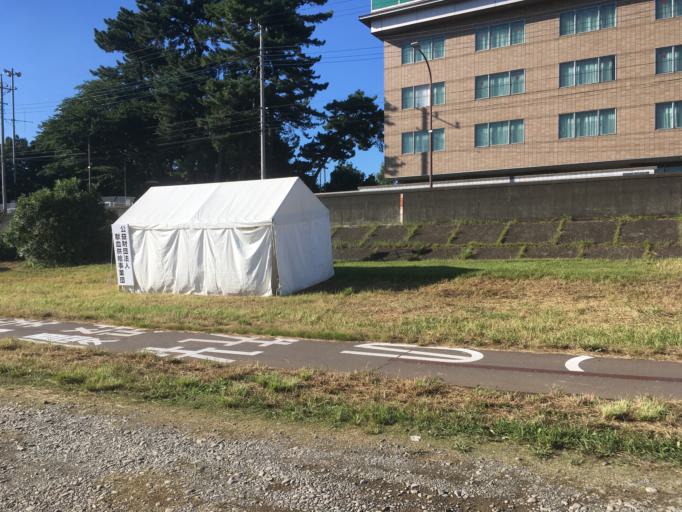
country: JP
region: Tokyo
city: Chofugaoka
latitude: 35.6423
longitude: 139.5318
